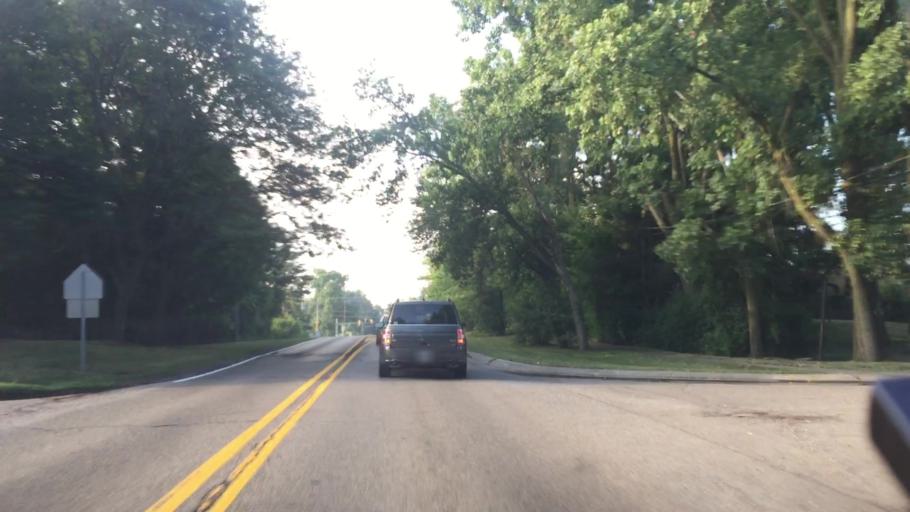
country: US
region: Michigan
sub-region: Oakland County
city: Bloomfield Hills
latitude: 42.6003
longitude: -83.2478
